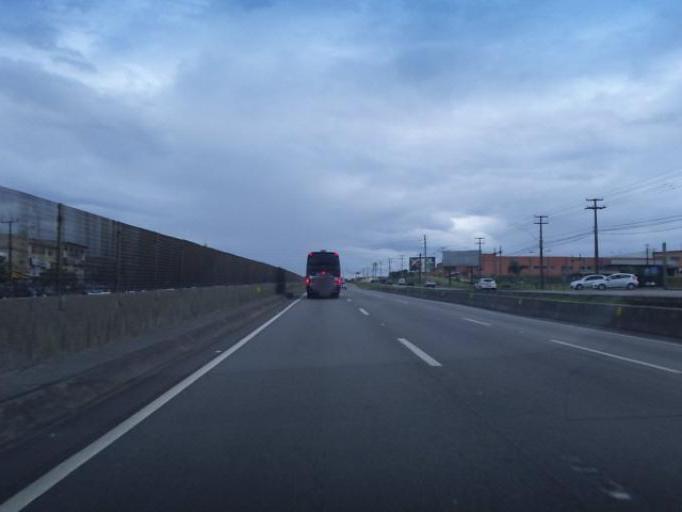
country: BR
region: Parana
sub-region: Sao Jose Dos Pinhais
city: Sao Jose dos Pinhais
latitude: -25.6044
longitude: -49.1729
